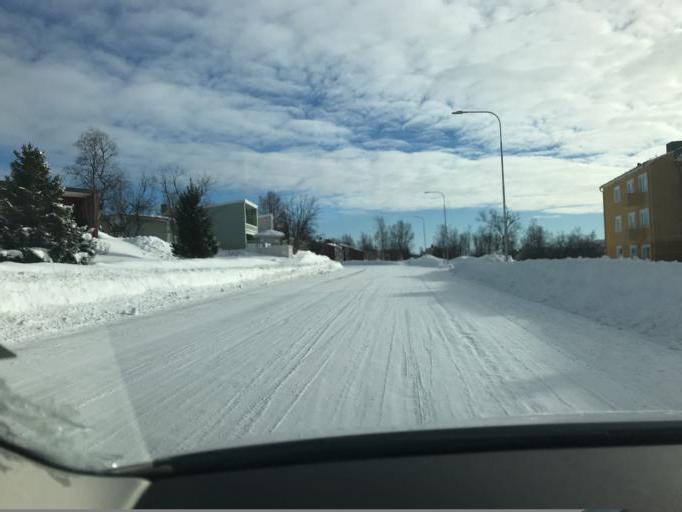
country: SE
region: Norrbotten
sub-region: Kiruna Kommun
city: Kiruna
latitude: 67.8646
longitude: 20.2083
